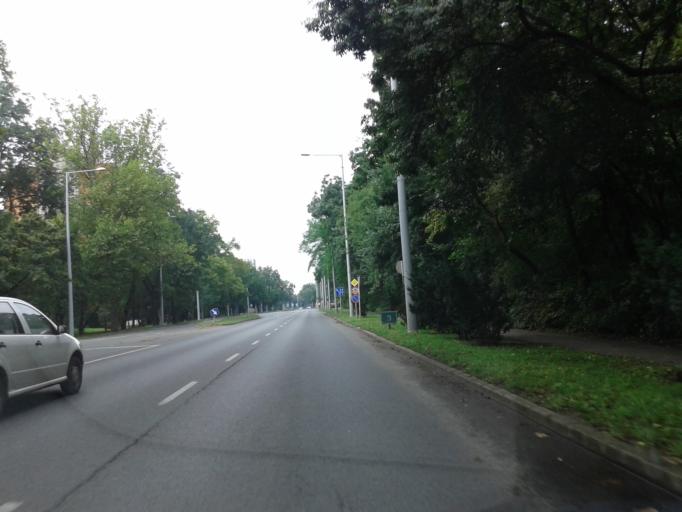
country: HU
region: Csongrad
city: Szeged
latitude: 46.2487
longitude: 20.1662
